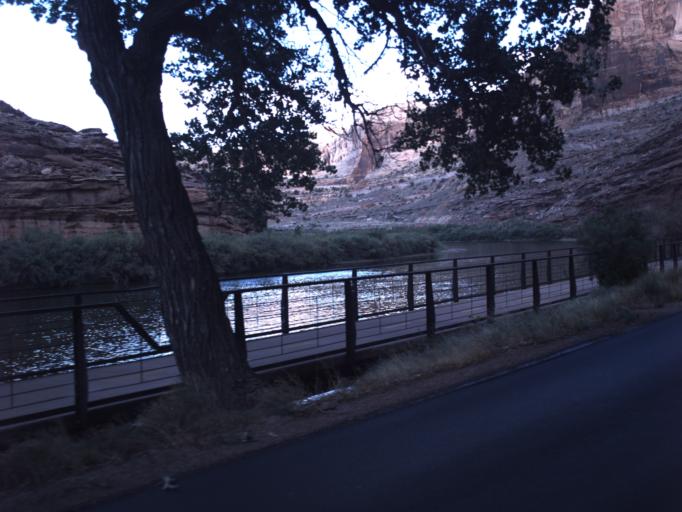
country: US
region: Utah
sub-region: Grand County
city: Moab
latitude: 38.6021
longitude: -109.5682
